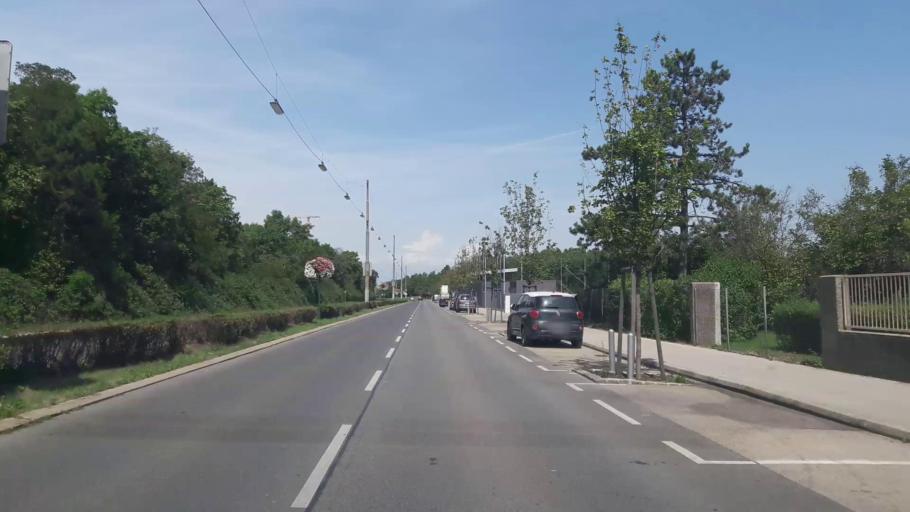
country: AT
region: Lower Austria
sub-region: Politischer Bezirk Wien-Umgebung
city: Leopoldsdorf
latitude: 48.1582
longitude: 16.3948
